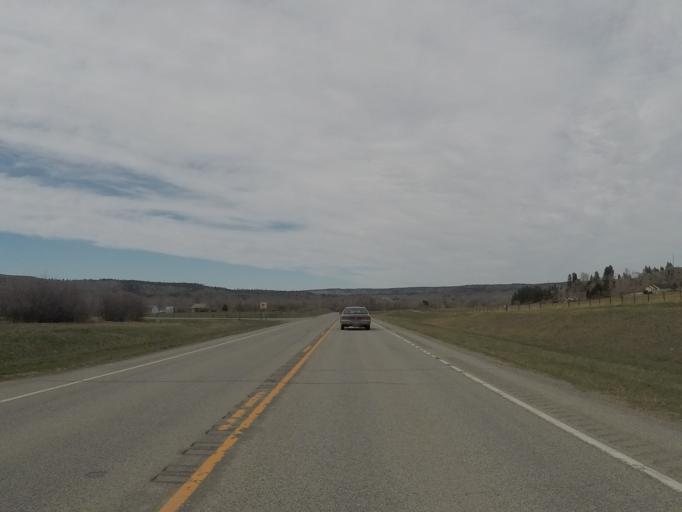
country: US
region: Montana
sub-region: Stillwater County
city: Columbus
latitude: 45.6231
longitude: -109.2790
